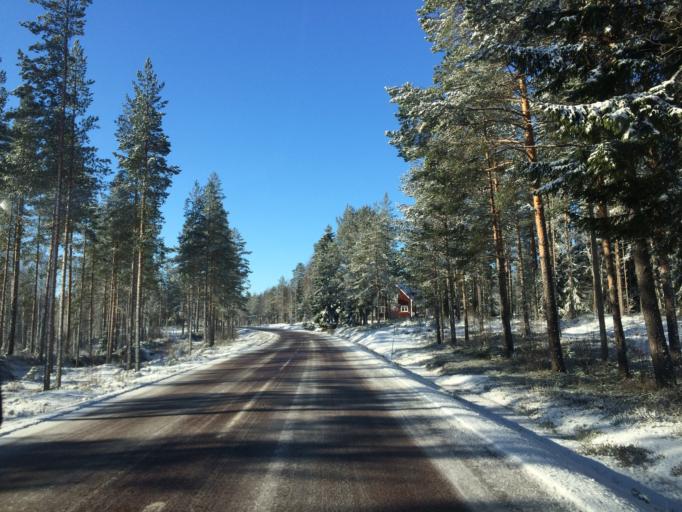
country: SE
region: Dalarna
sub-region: Vansbro Kommun
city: Vansbro
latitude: 60.7377
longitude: 14.1259
